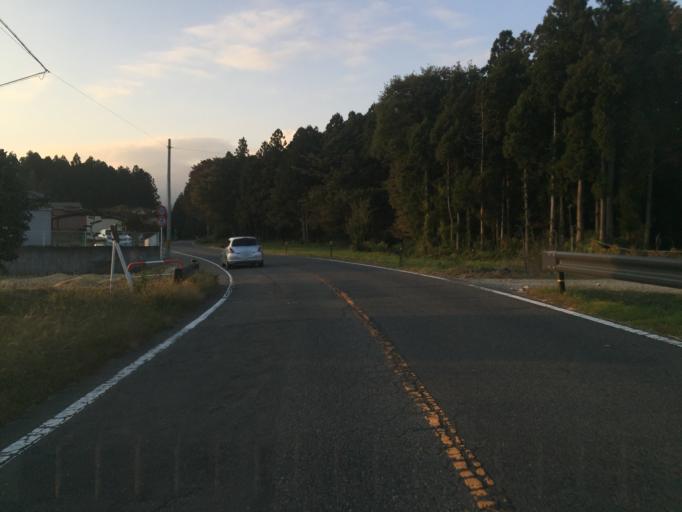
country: JP
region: Fukushima
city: Motomiya
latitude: 37.5525
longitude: 140.3609
